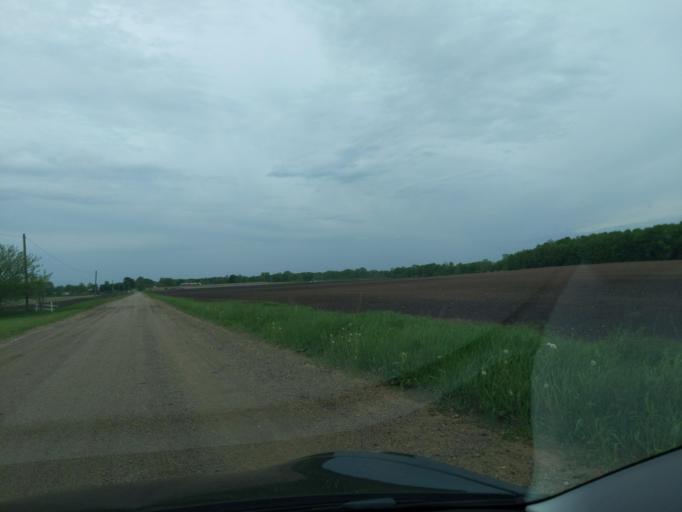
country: US
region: Michigan
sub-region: Ingham County
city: Stockbridge
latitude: 42.4209
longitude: -84.2141
